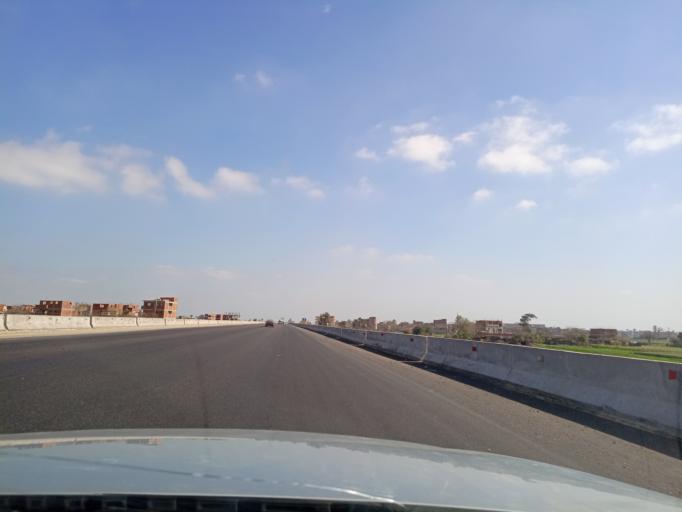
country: EG
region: Muhafazat al Minufiyah
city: Al Bajur
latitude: 30.4144
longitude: 31.0663
